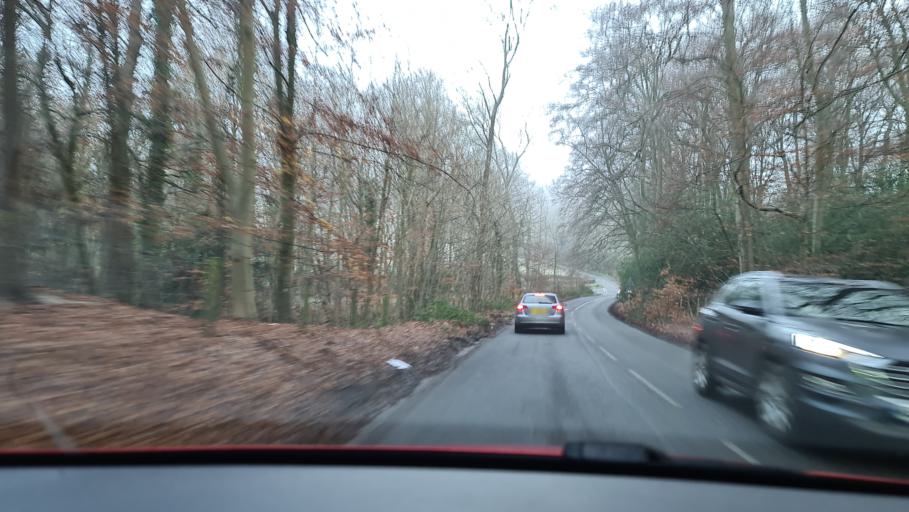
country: GB
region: England
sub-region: Buckinghamshire
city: Seer Green
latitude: 51.6071
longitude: -0.5974
